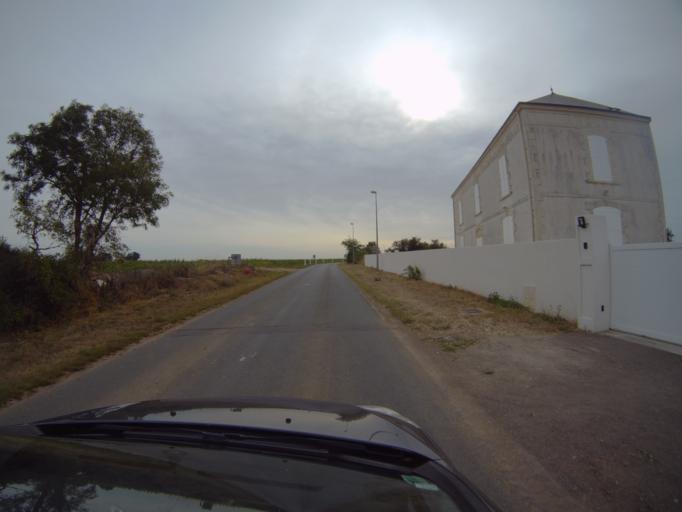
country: FR
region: Pays de la Loire
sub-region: Departement de la Vendee
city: Angles
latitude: 46.4067
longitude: -1.4172
